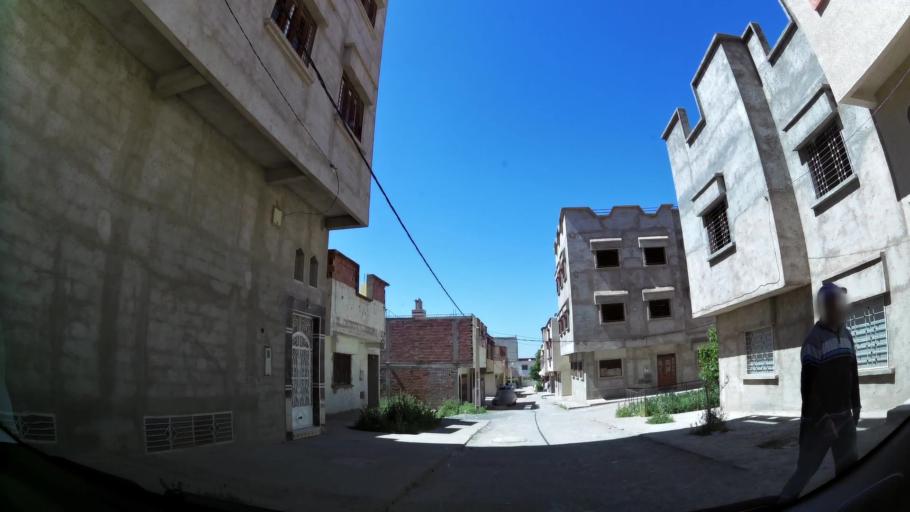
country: MA
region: Oriental
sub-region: Oujda-Angad
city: Oujda
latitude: 34.6590
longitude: -1.8762
